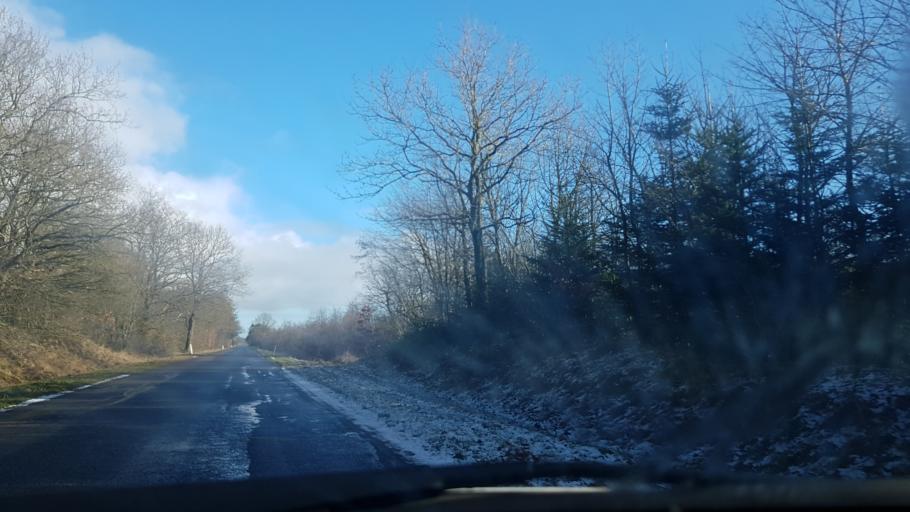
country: DK
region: South Denmark
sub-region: Haderslev Kommune
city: Vojens
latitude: 55.3200
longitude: 9.2285
